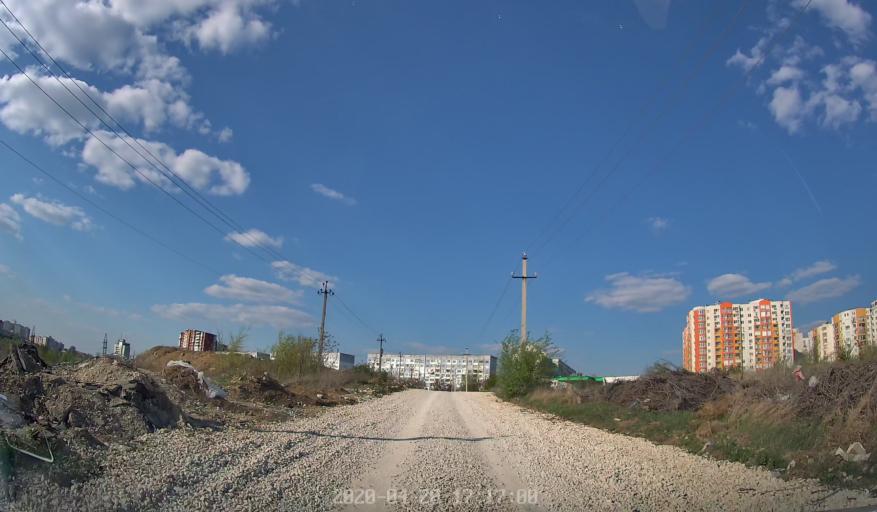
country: MD
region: Chisinau
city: Chisinau
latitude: 46.9727
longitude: 28.8464
